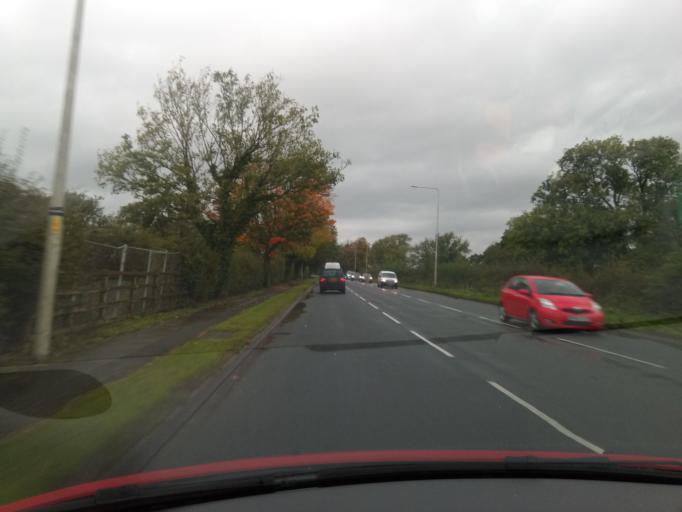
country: GB
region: England
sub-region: Lancashire
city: Catterall
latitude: 53.8446
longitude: -2.7431
